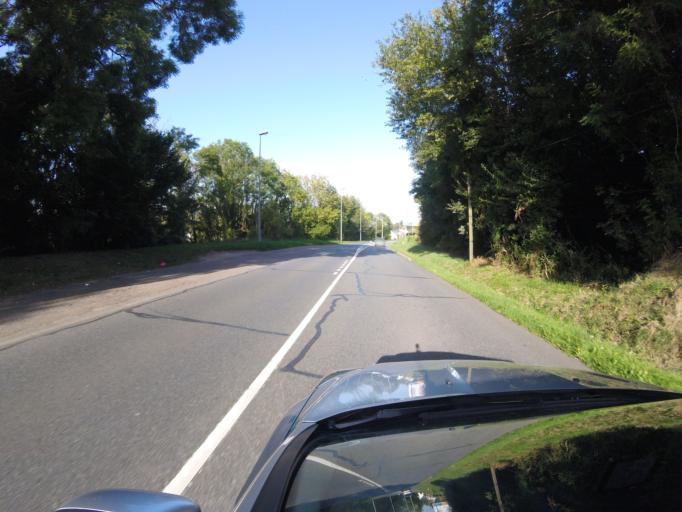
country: FR
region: Haute-Normandie
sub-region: Departement de la Seine-Maritime
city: Fecamp
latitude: 49.7597
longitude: 0.3889
